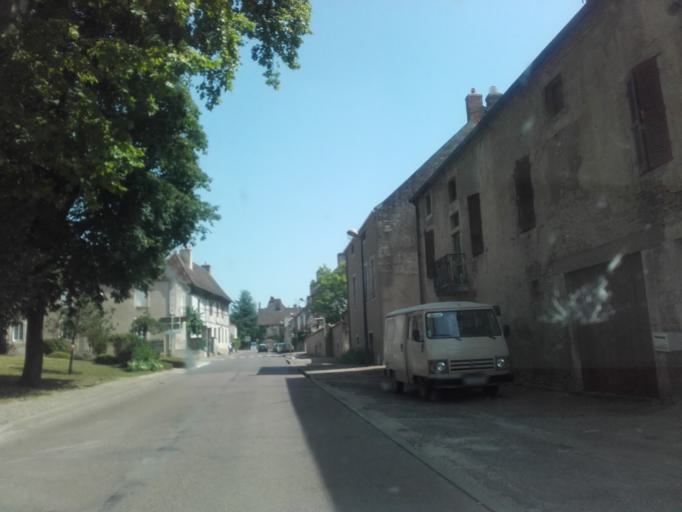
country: FR
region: Bourgogne
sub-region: Departement de Saone-et-Loire
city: Demigny
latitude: 46.9292
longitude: 4.8342
